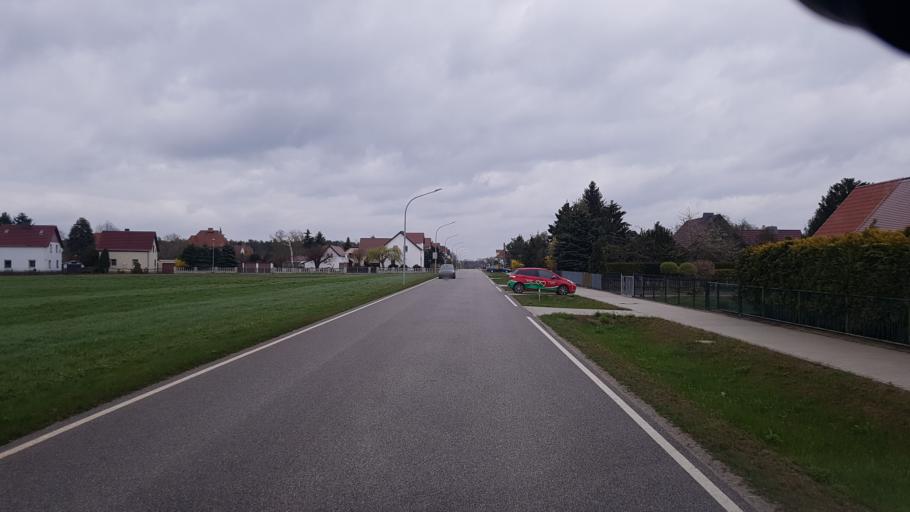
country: DE
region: Brandenburg
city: Hohenbocka
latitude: 51.4576
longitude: 14.0449
